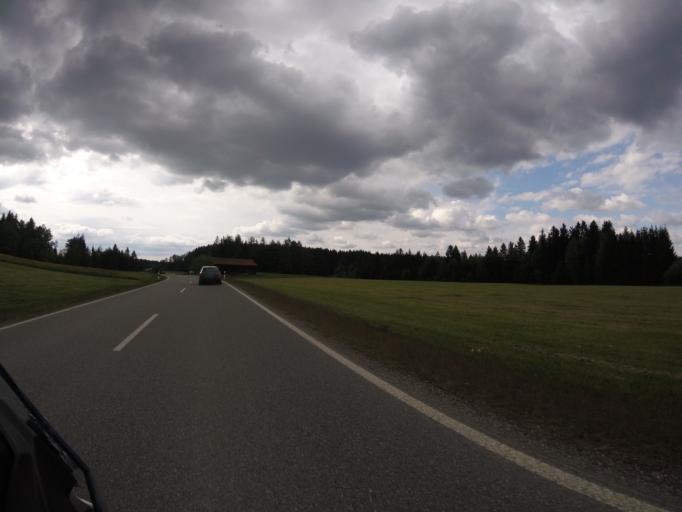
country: DE
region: Bavaria
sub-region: Upper Bavaria
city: Dietramszell
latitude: 47.8578
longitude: 11.5792
